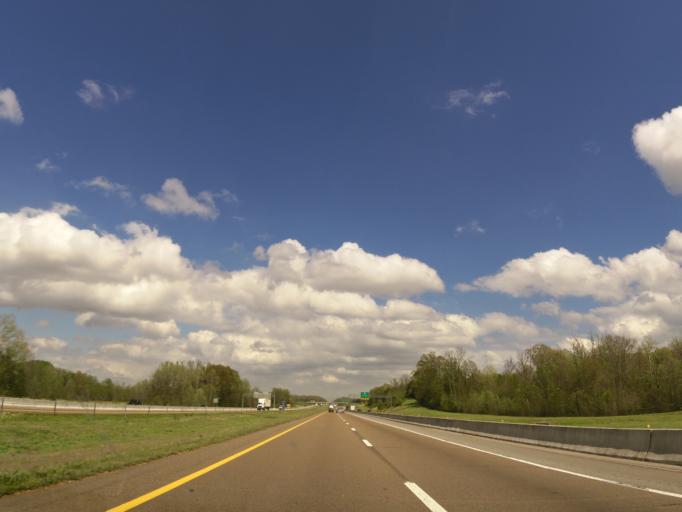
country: US
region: Tennessee
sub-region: Shelby County
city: Arlington
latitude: 35.2569
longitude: -89.6751
